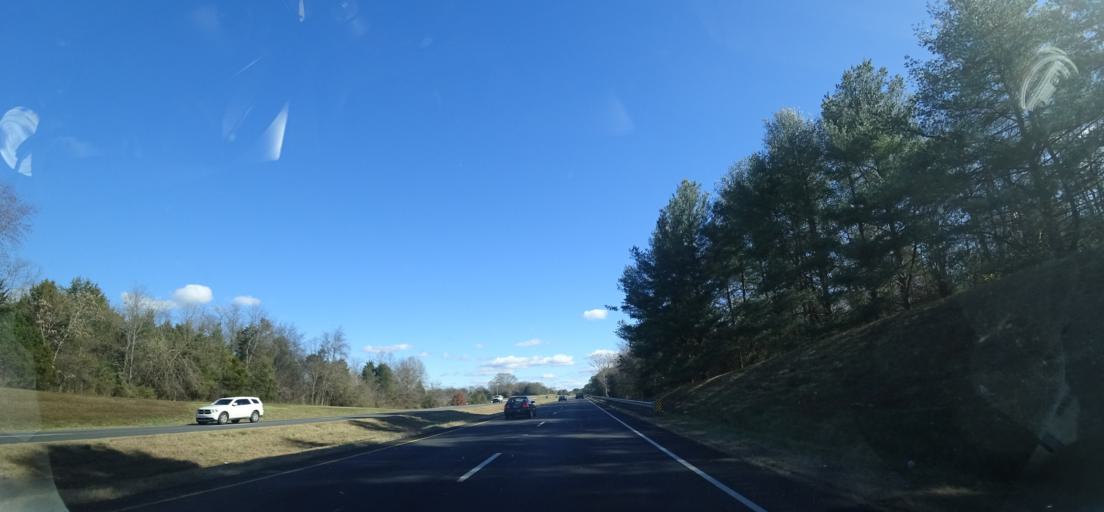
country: US
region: Virginia
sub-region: Culpeper County
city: Culpeper
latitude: 38.5010
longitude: -77.9102
